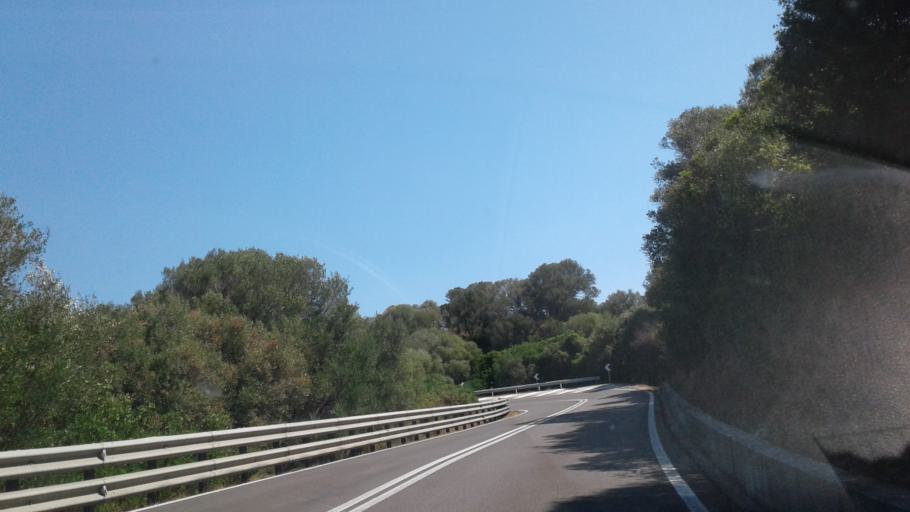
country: IT
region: Sardinia
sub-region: Provincia di Olbia-Tempio
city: Palau
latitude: 41.1684
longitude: 9.3176
